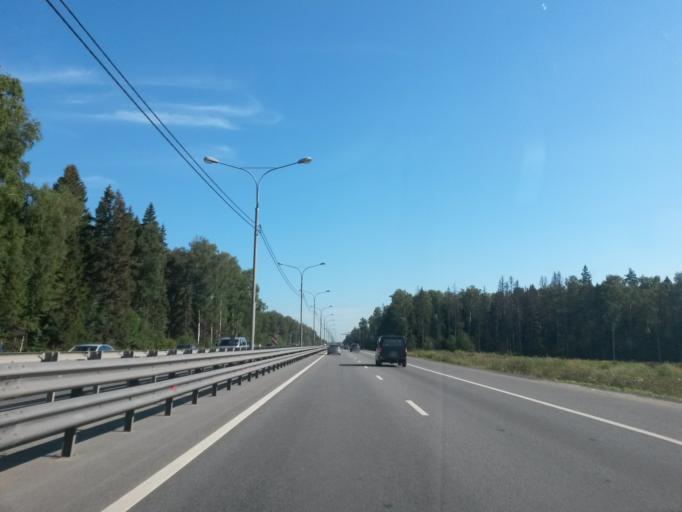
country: RU
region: Moskovskaya
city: Pushkino
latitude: 56.0264
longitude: 37.8852
